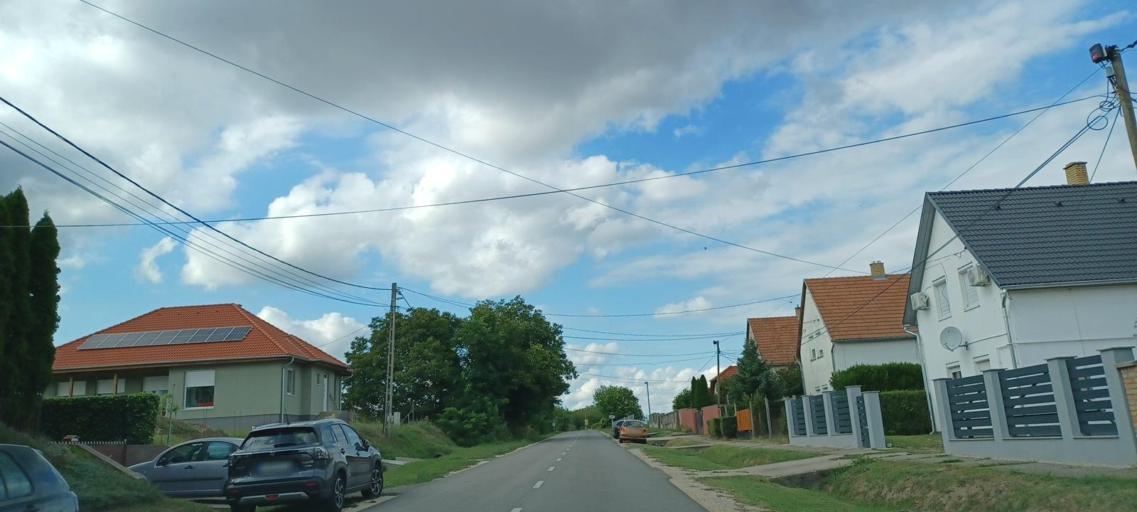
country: HU
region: Tolna
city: Szentgalpuszta
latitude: 46.4054
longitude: 18.6165
